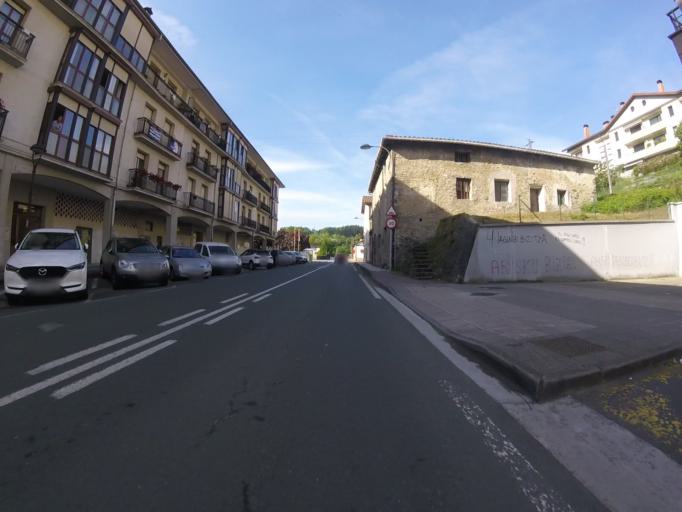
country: ES
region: Basque Country
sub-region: Provincia de Guipuzcoa
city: Isasondo
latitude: 43.0679
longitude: -2.1646
